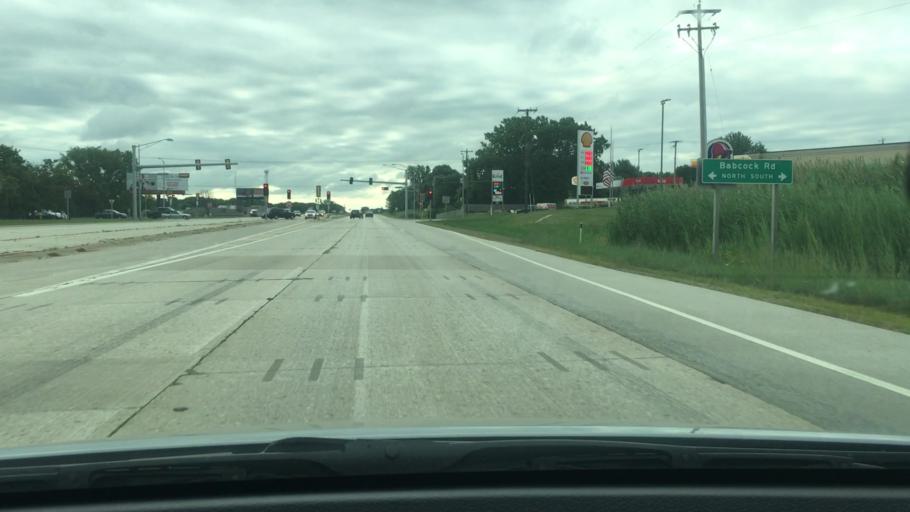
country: US
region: Wisconsin
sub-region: Brown County
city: Ashwaubenon
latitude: 44.4927
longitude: -88.0995
